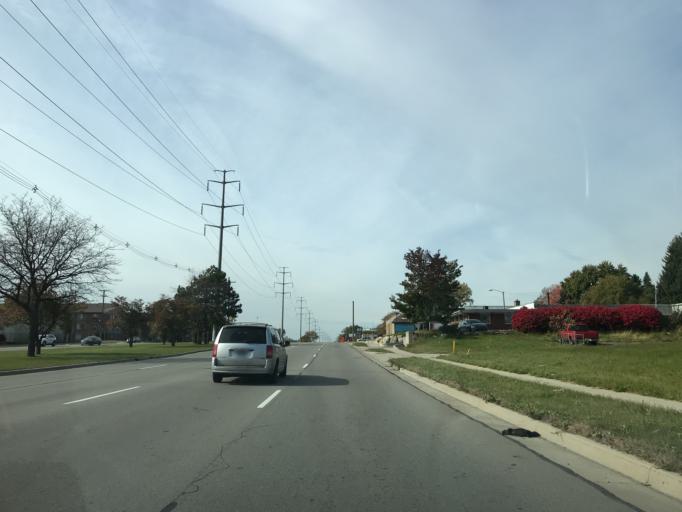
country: US
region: Michigan
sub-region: Oakland County
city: Southfield
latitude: 42.4433
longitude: -83.2710
